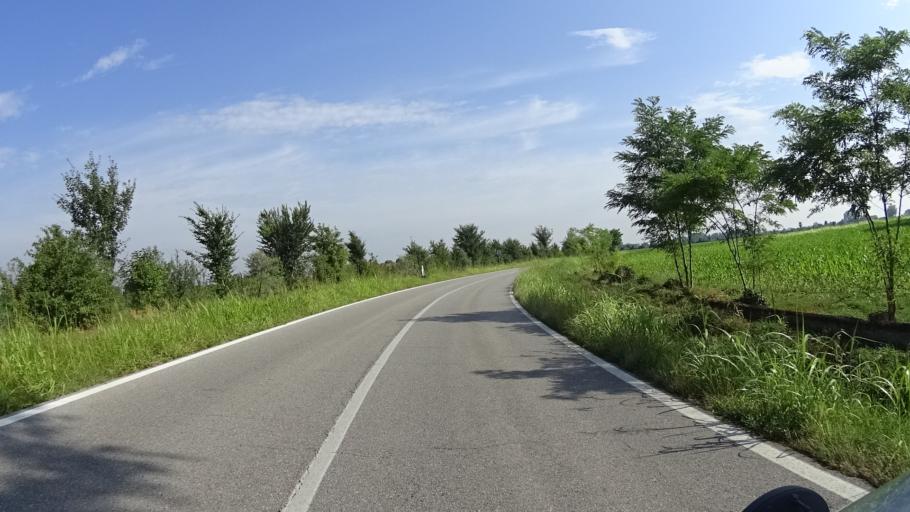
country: IT
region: Veneto
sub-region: Provincia di Venezia
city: Lugugnana
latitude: 45.7150
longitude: 12.9486
